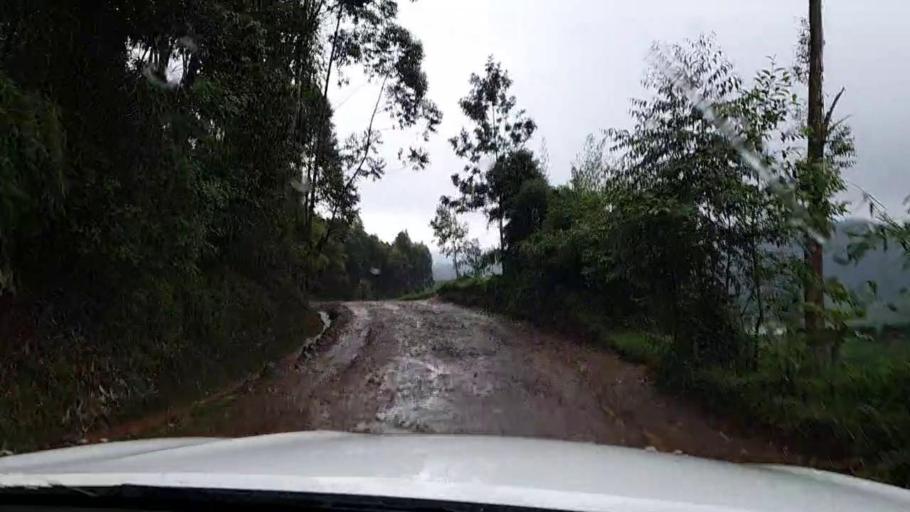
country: RW
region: Western Province
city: Cyangugu
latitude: -2.4632
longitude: 29.0338
